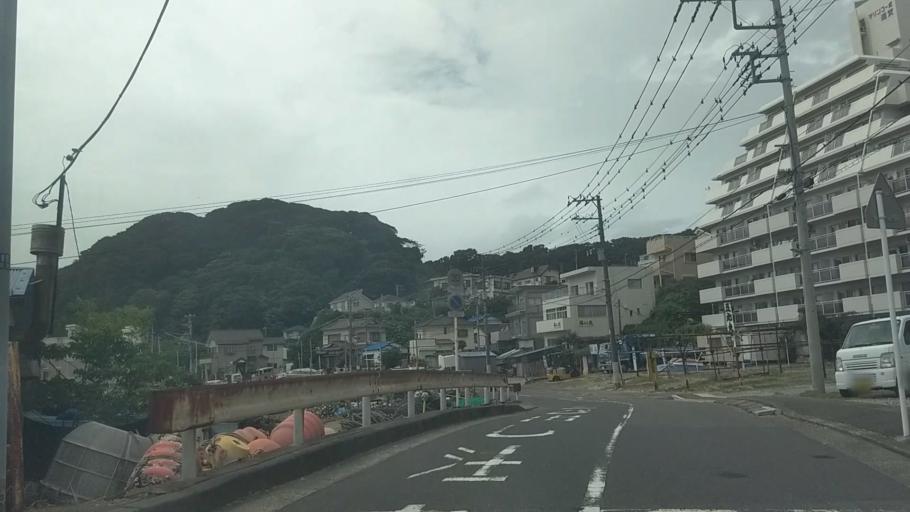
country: JP
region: Kanagawa
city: Yokosuka
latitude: 35.2422
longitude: 139.7277
